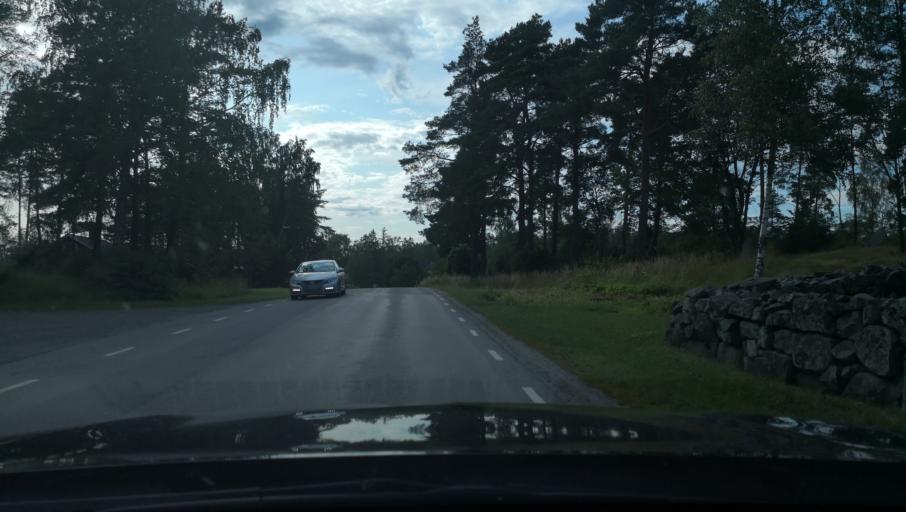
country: SE
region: Uppsala
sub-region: Enkopings Kommun
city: Orsundsbro
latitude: 59.6883
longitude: 17.3847
